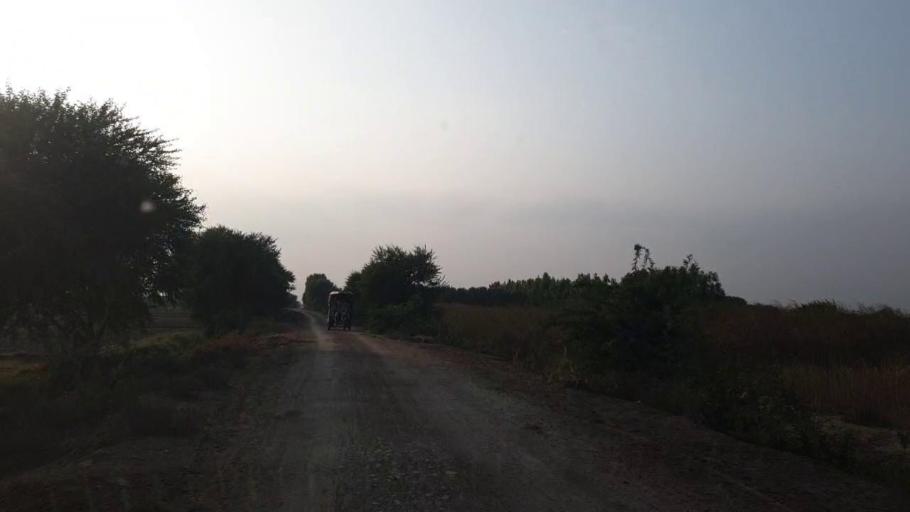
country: PK
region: Sindh
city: Rajo Khanani
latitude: 25.0352
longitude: 68.9737
